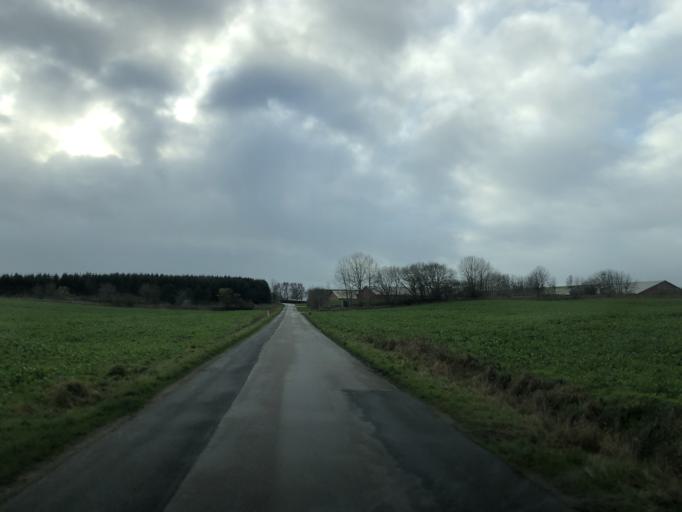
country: DK
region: North Denmark
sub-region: Rebild Kommune
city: Stovring
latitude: 56.9227
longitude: 9.8043
